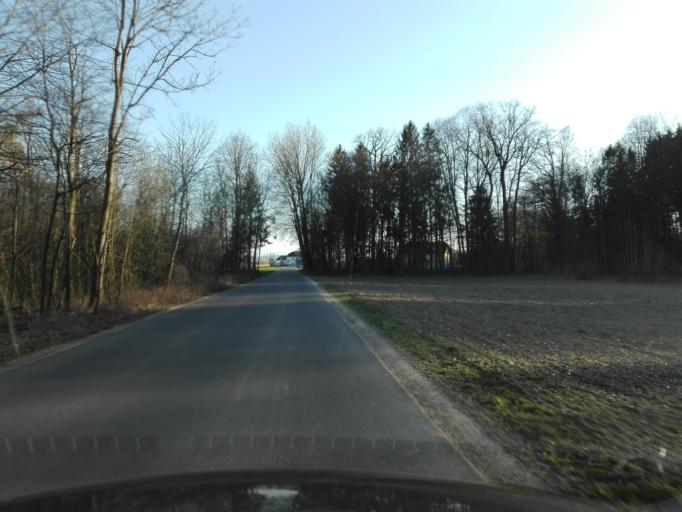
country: AT
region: Upper Austria
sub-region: Politischer Bezirk Perg
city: Perg
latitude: 48.2092
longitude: 14.6899
